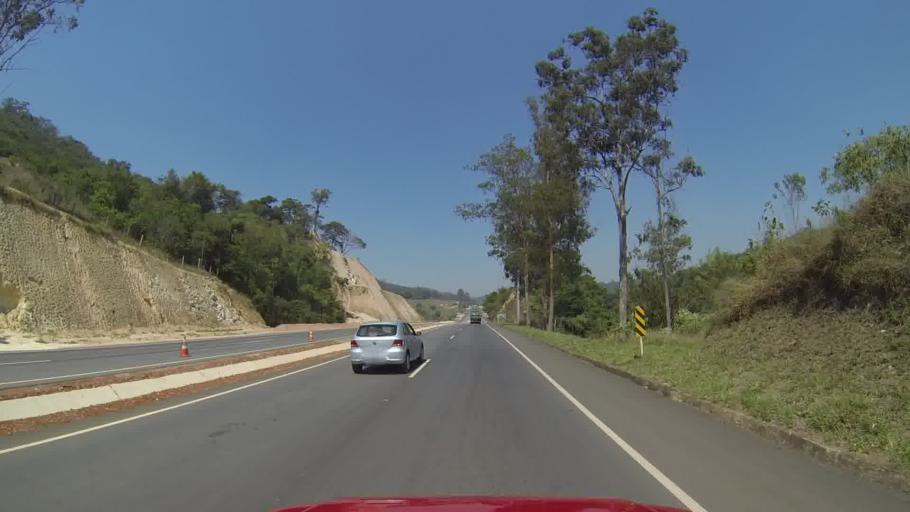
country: BR
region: Minas Gerais
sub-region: Mateus Leme
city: Mateus Leme
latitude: -20.0160
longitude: -44.4900
